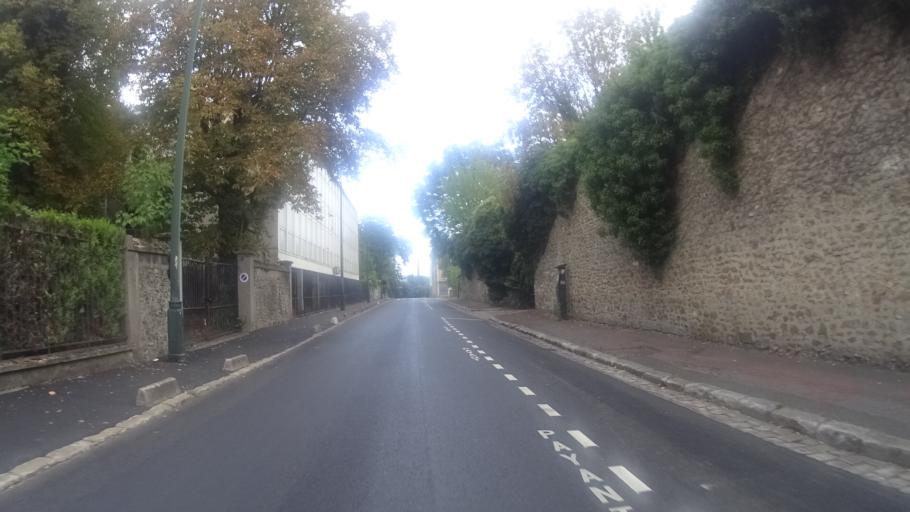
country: FR
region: Ile-de-France
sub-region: Departement de l'Essonne
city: Saint-Germain-les-Corbeil
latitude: 48.6148
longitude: 2.4760
